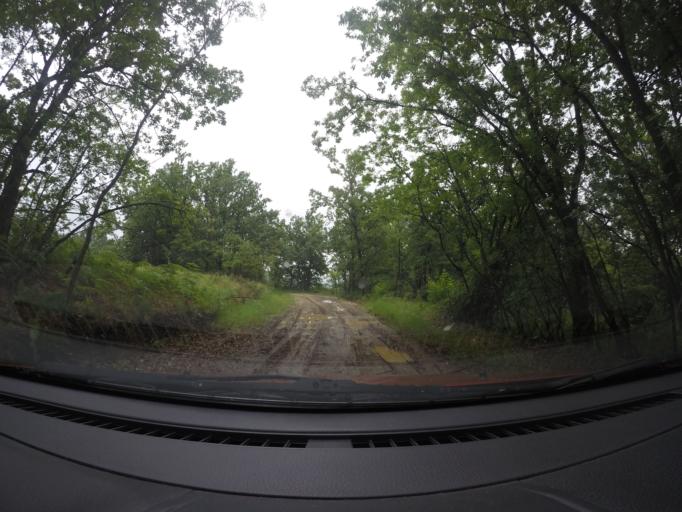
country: RS
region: Central Serbia
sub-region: Belgrade
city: Sopot
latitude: 44.5458
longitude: 20.5092
